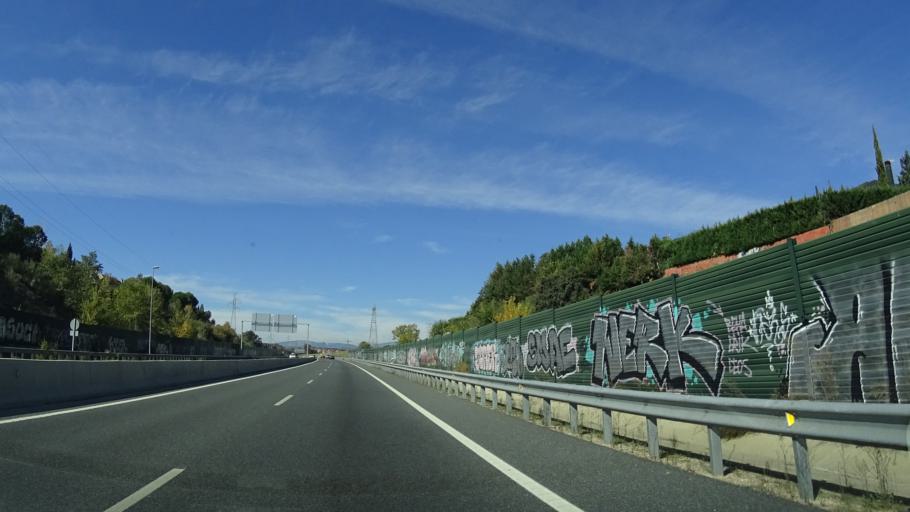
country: ES
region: Madrid
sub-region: Provincia de Madrid
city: Villanueva del Pardillo
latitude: 40.4882
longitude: -3.9477
